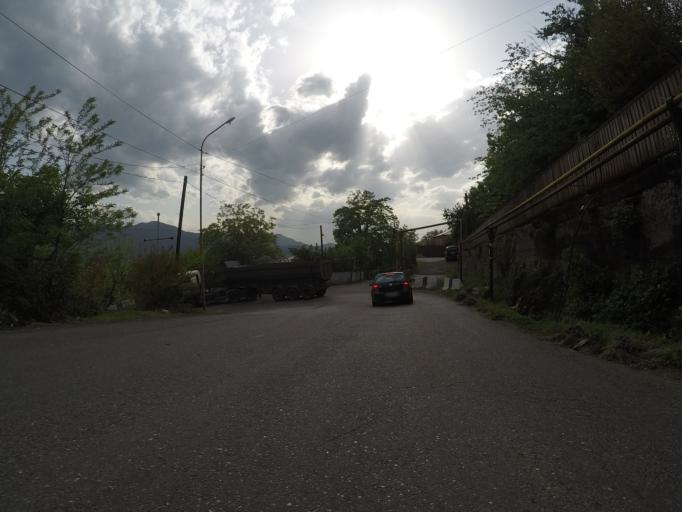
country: GE
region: Imereti
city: Zestap'oni
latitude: 42.1140
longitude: 43.0477
